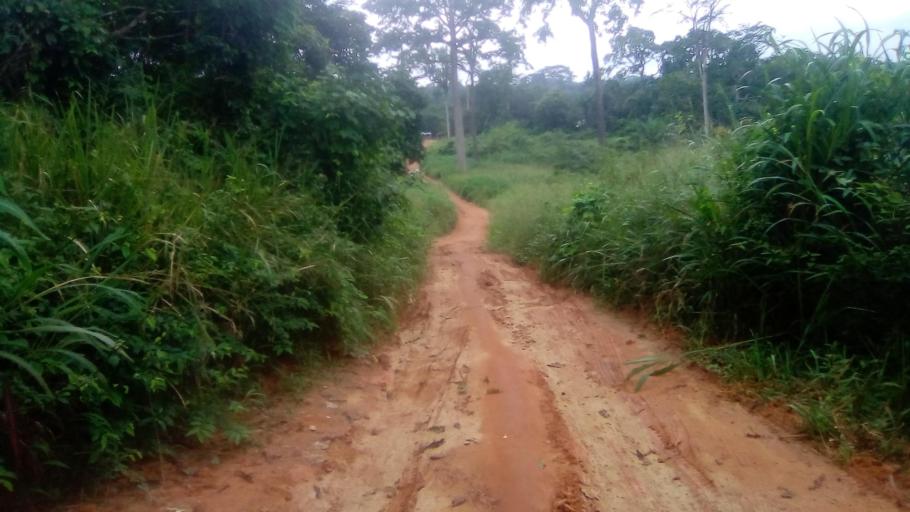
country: SL
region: Eastern Province
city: Kailahun
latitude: 8.3076
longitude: -10.5601
